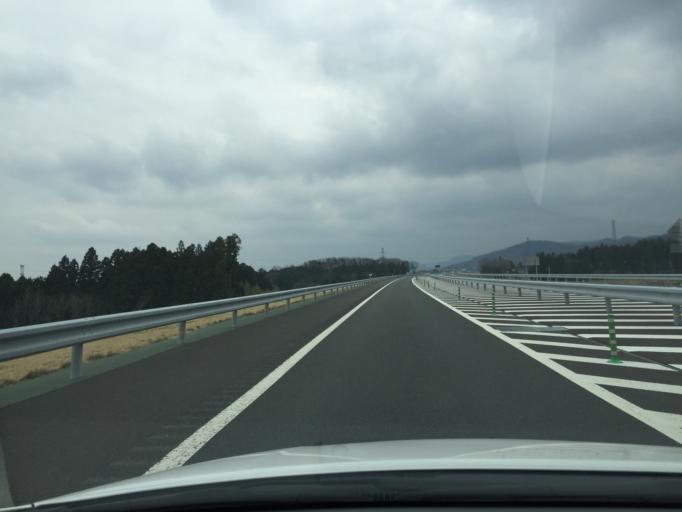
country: JP
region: Miyagi
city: Marumori
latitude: 37.8641
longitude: 140.8828
